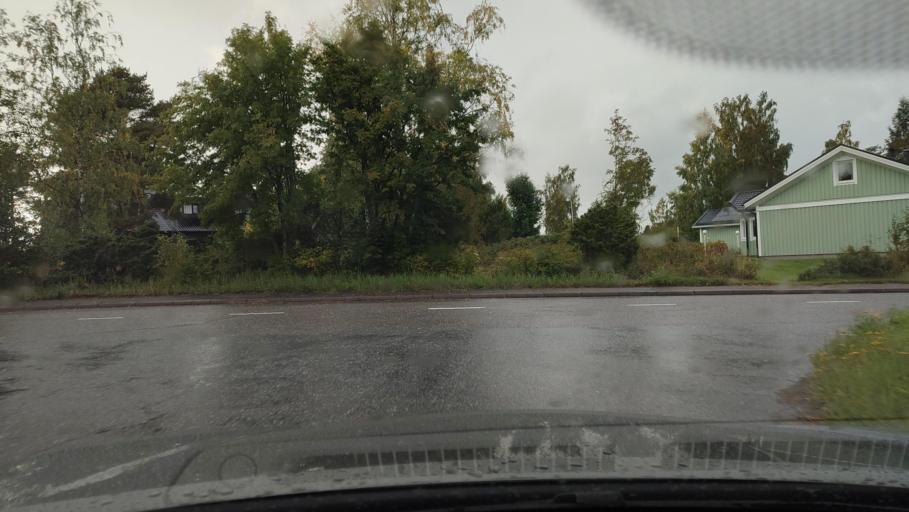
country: FI
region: Ostrobothnia
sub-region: Sydosterbotten
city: Kristinestad
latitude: 62.2812
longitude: 21.3757
